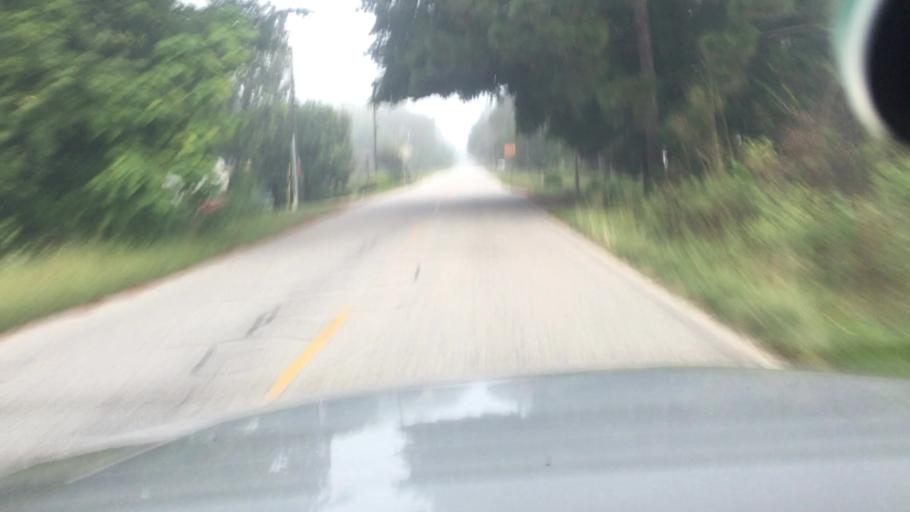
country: US
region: North Carolina
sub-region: Cumberland County
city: Fayetteville
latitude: 35.0155
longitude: -78.9122
